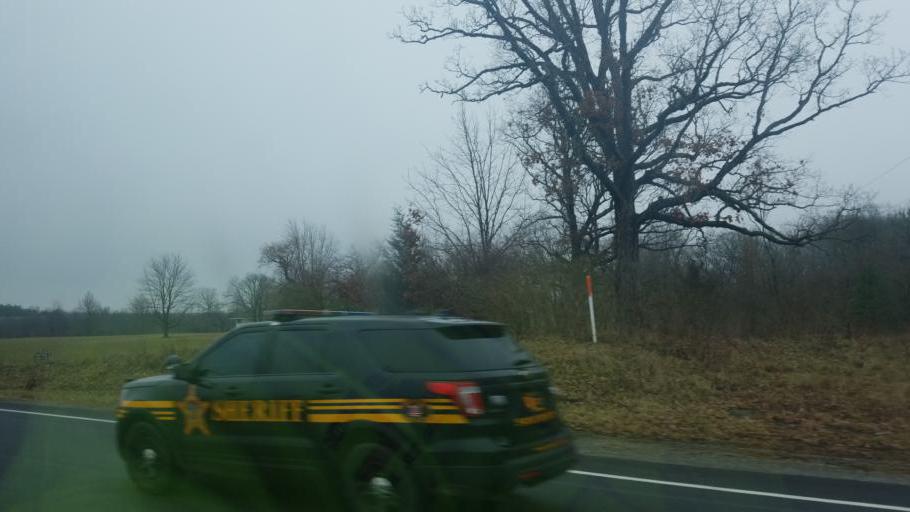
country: US
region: Ohio
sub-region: Union County
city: Marysville
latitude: 40.2454
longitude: -83.4054
